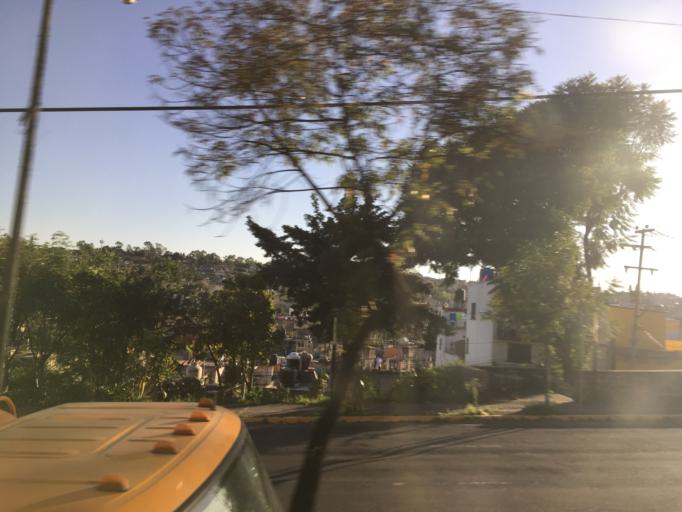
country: MX
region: Mexico City
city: Polanco
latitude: 19.3967
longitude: -99.2088
